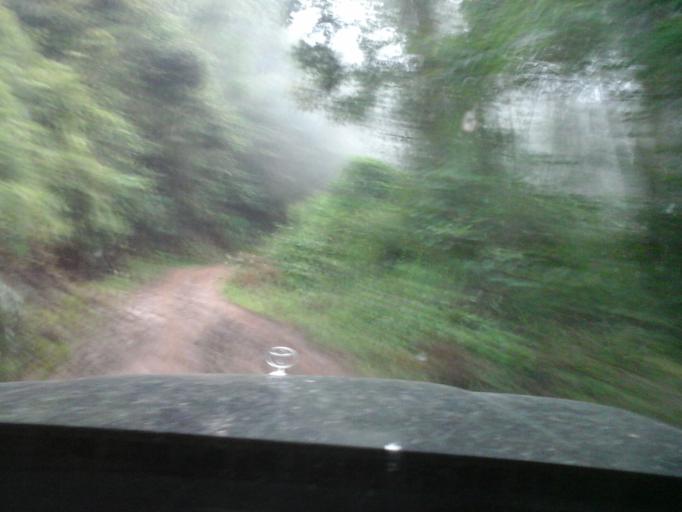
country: CO
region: Cesar
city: Agustin Codazzi
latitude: 9.9395
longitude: -73.1374
